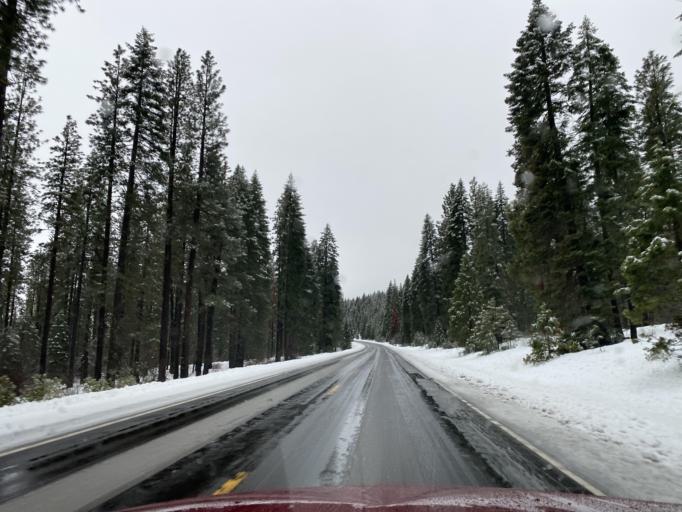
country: US
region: Oregon
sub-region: Klamath County
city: Klamath Falls
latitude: 42.5409
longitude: -122.0892
